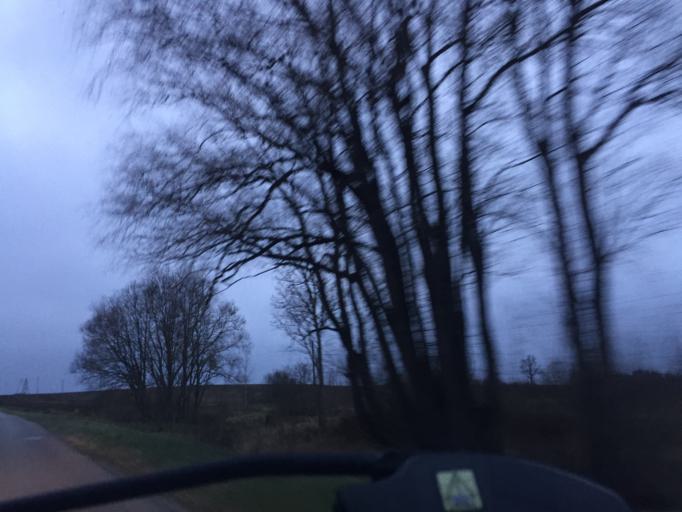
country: LV
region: Limbazu Rajons
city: Limbazi
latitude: 57.6178
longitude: 24.8319
